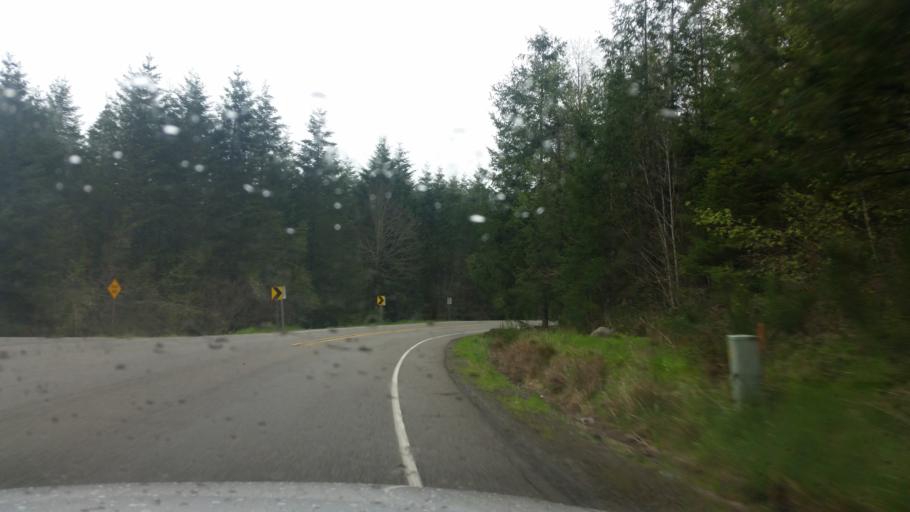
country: US
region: Washington
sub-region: Pierce County
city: Eatonville
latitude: 46.8649
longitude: -122.3258
